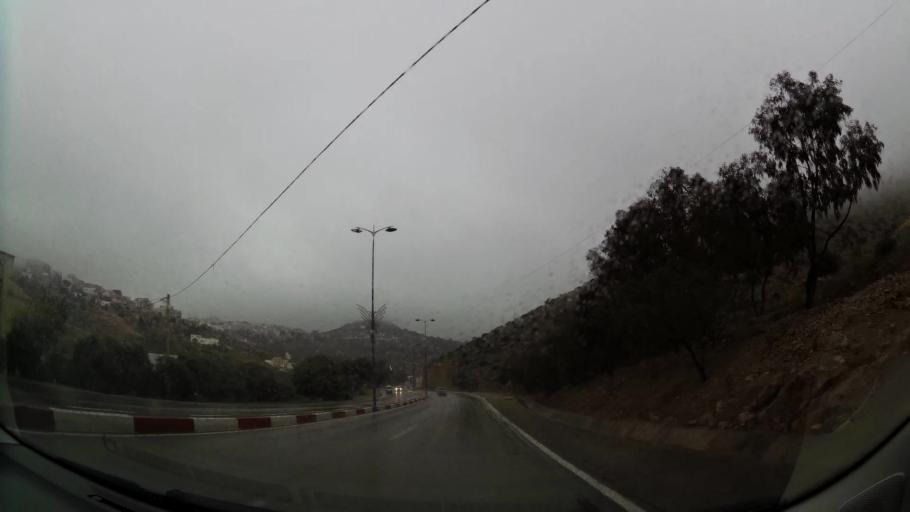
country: MA
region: Taza-Al Hoceima-Taounate
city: Al Hoceima
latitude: 35.2273
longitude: -3.9307
